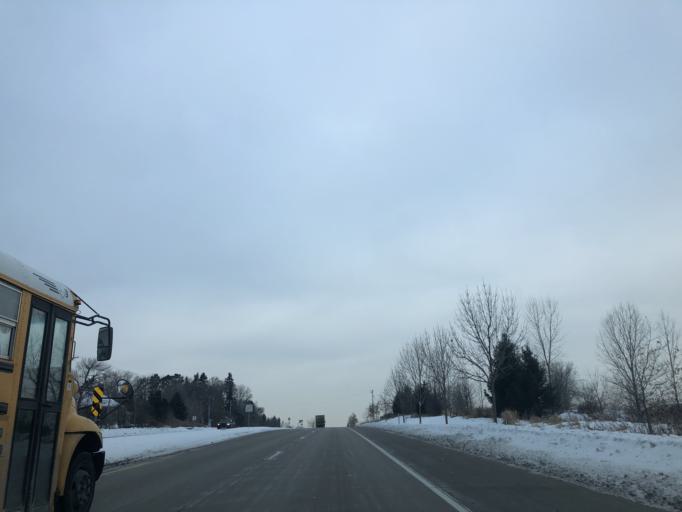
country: US
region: Minnesota
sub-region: Ramsey County
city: Shoreview
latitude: 45.0794
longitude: -93.1611
